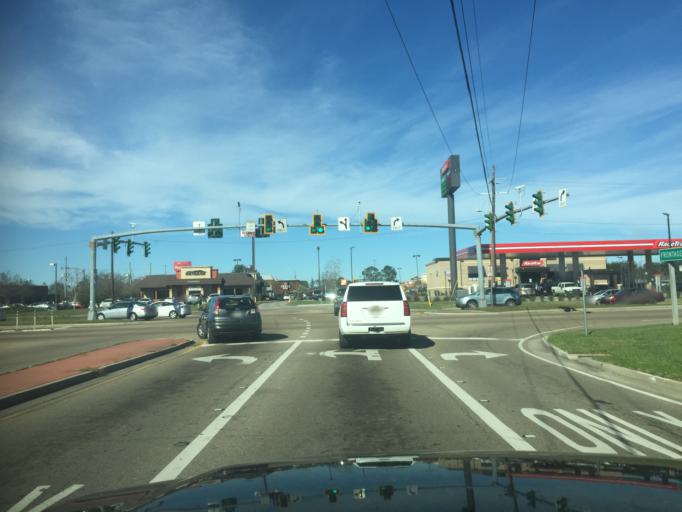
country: US
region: Louisiana
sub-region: Saint Tammany Parish
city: Slidell
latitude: 30.2845
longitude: -89.7475
